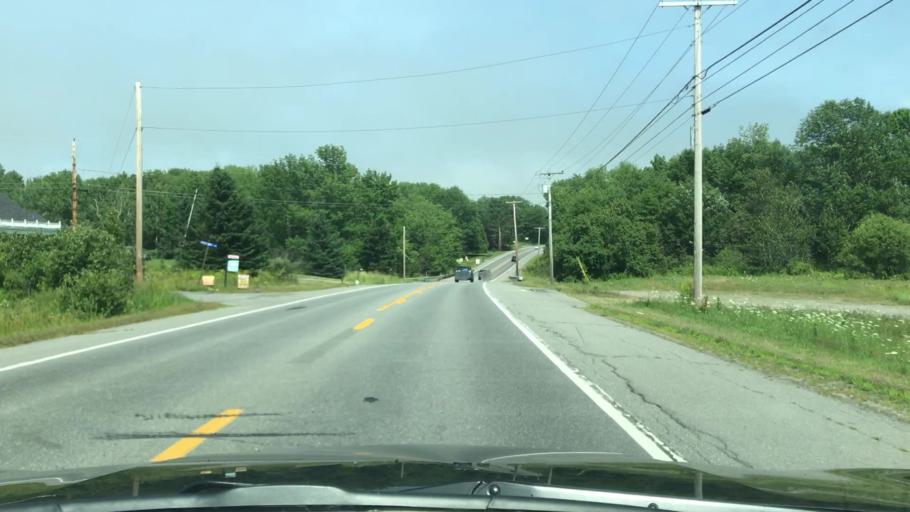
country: US
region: Maine
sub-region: Waldo County
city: Belfast
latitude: 44.4331
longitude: -68.9560
